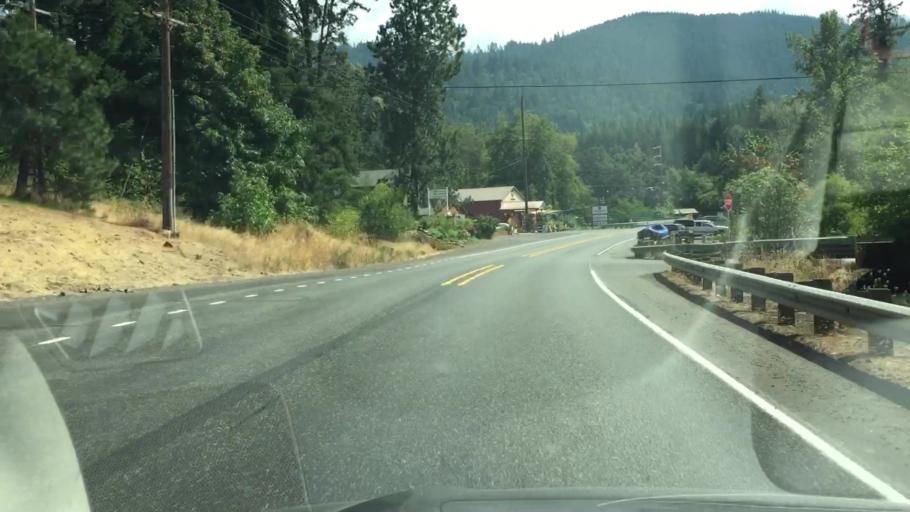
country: US
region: Washington
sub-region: Klickitat County
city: White Salmon
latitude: 45.7985
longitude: -121.4854
